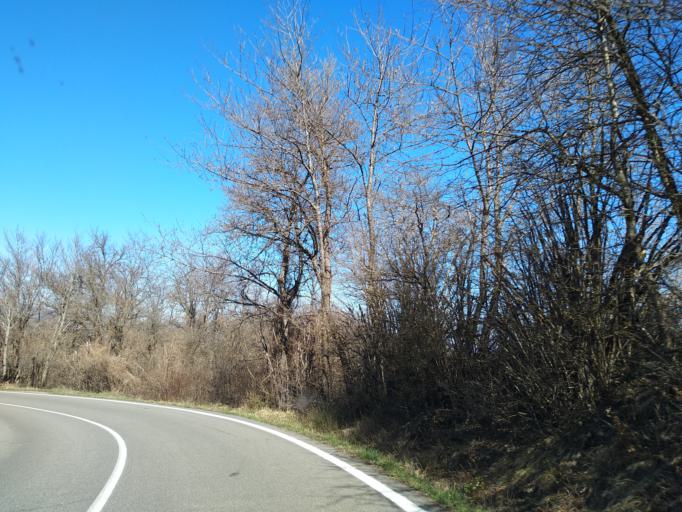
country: IT
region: Emilia-Romagna
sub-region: Provincia di Reggio Emilia
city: Busana
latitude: 44.4053
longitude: 10.3180
